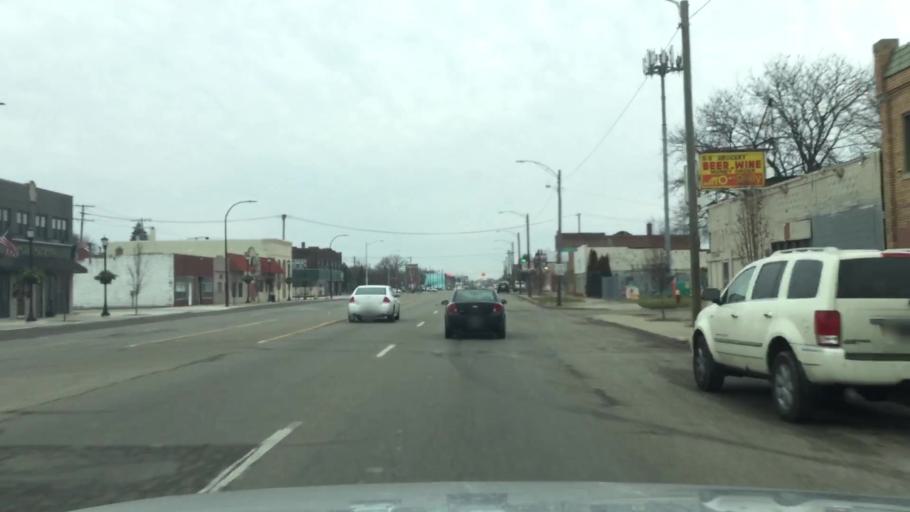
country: US
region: Michigan
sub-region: Wayne County
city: Grosse Pointe Park
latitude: 42.3880
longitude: -82.9439
